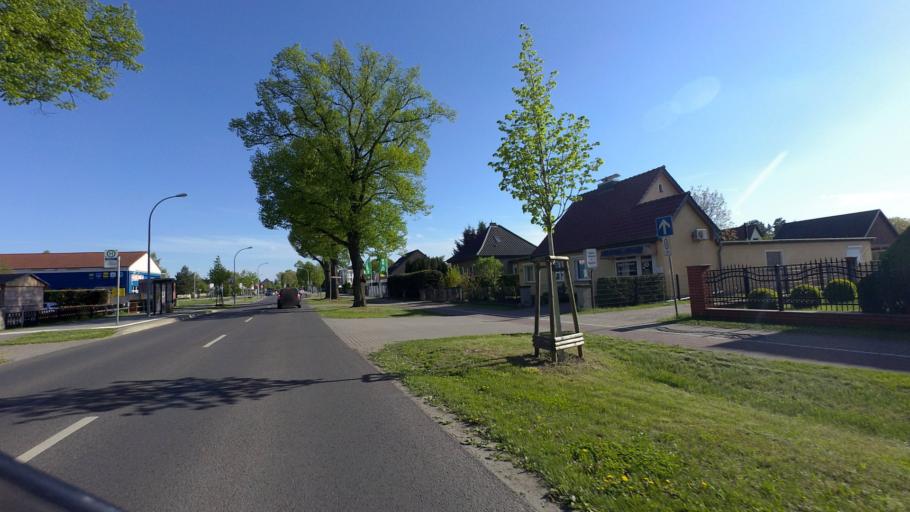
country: DE
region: Brandenburg
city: Oranienburg
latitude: 52.7342
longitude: 13.2435
